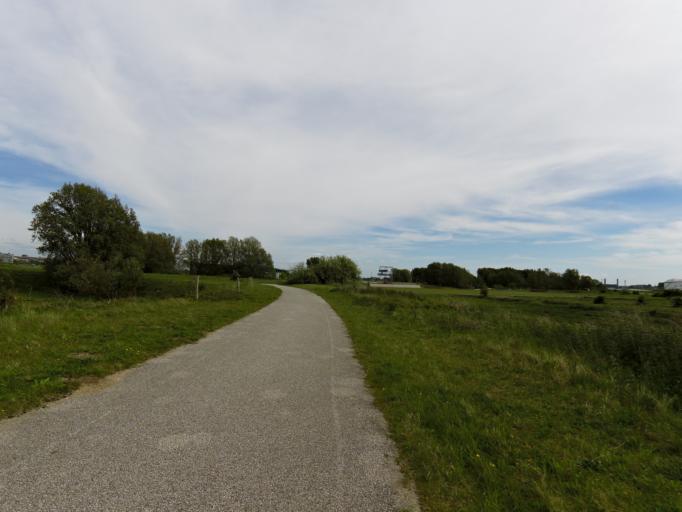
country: NL
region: South Holland
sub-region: Gemeente Maassluis
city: Maassluis
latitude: 51.9252
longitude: 4.2193
